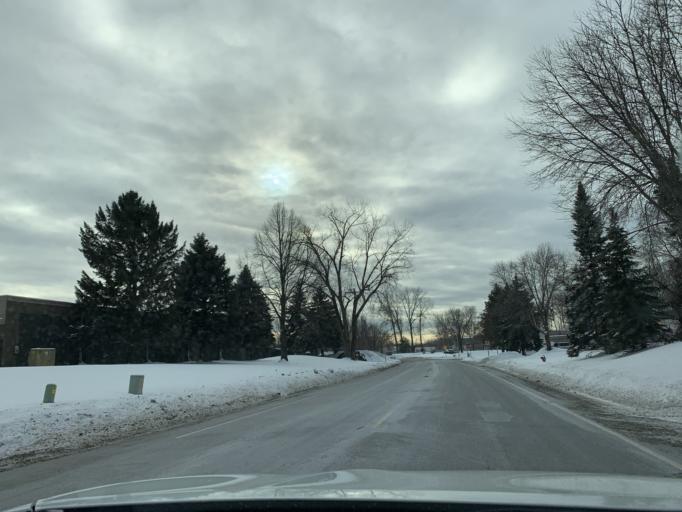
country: US
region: Minnesota
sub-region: Anoka County
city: Andover
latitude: 45.1788
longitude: -93.2981
